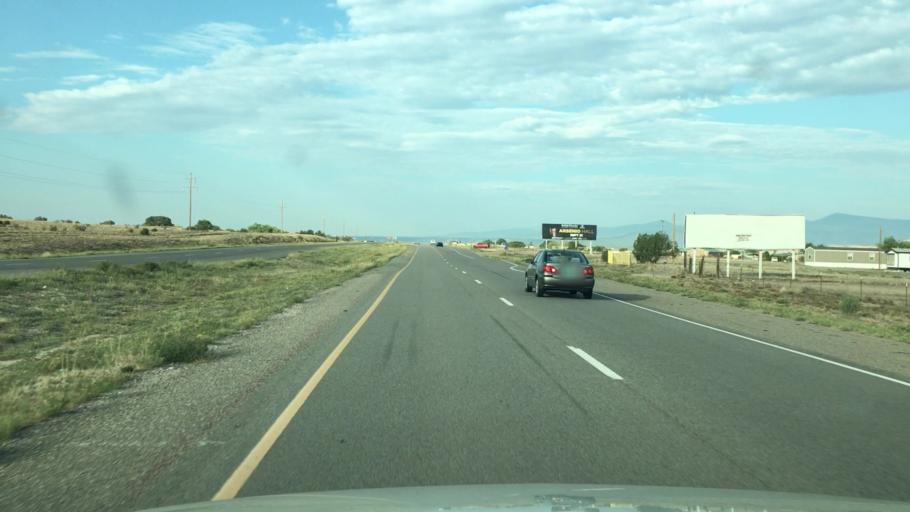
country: US
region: New Mexico
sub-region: Rio Arriba County
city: Ohkay Owingeh
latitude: 36.1198
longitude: -106.0156
